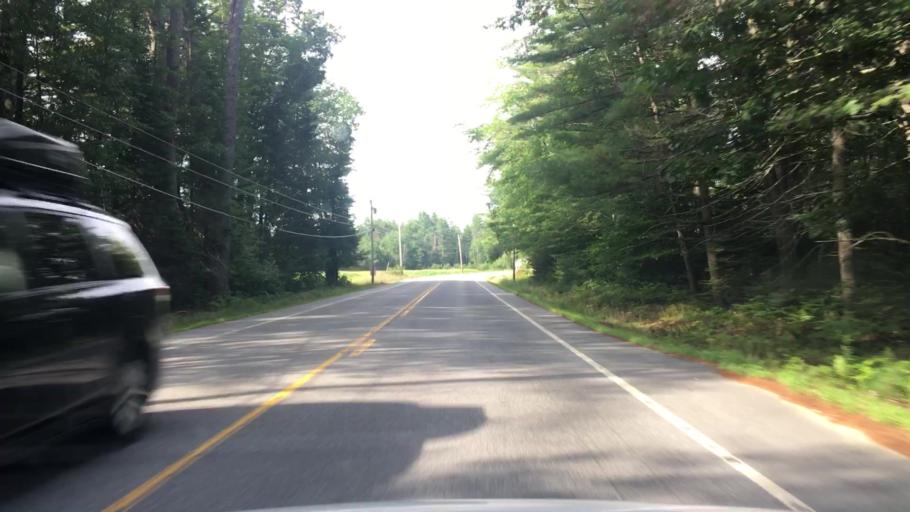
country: US
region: Maine
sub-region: Oxford County
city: Porter
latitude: 43.7913
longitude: -70.9499
